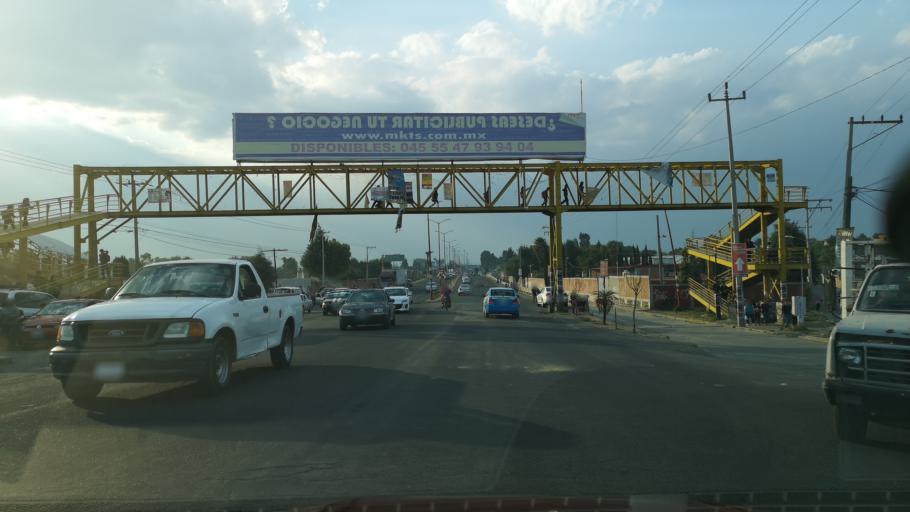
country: MX
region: Puebla
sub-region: Juan C. Bonilla
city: Santa Maria Zacatepec
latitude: 19.1233
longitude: -98.3655
